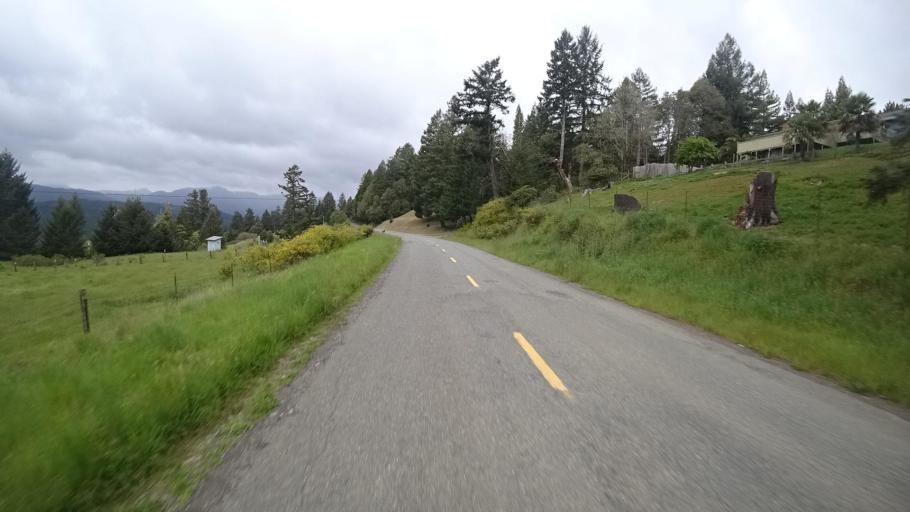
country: US
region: California
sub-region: Humboldt County
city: Redway
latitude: 40.2899
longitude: -123.8055
